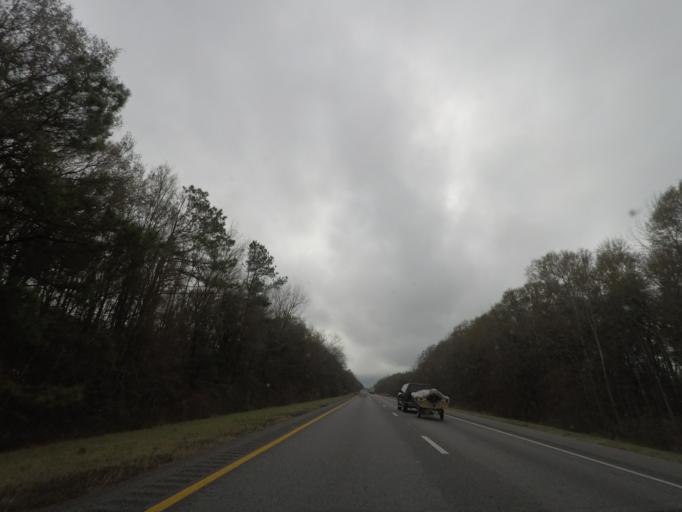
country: US
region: South Carolina
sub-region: Orangeburg County
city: Holly Hill
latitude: 33.3474
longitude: -80.5324
